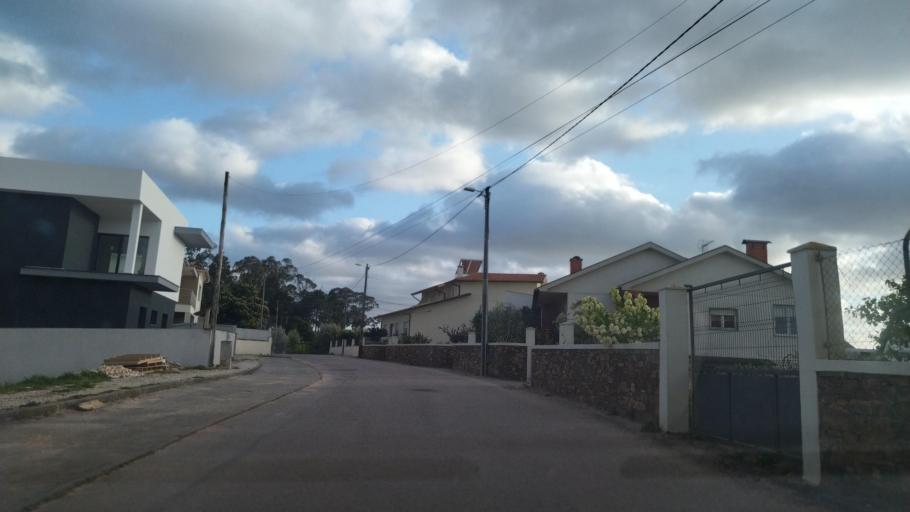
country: PT
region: Coimbra
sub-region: Coimbra
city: Coimbra
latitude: 40.1723
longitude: -8.4433
